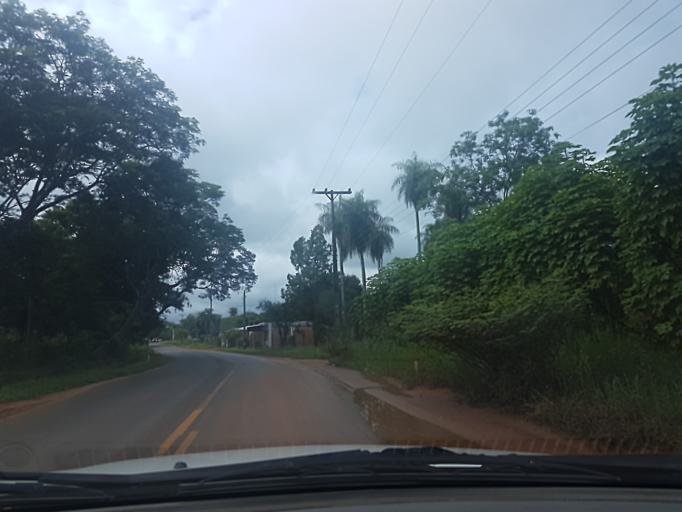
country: PY
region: Central
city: Limpio
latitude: -25.2277
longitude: -57.4493
